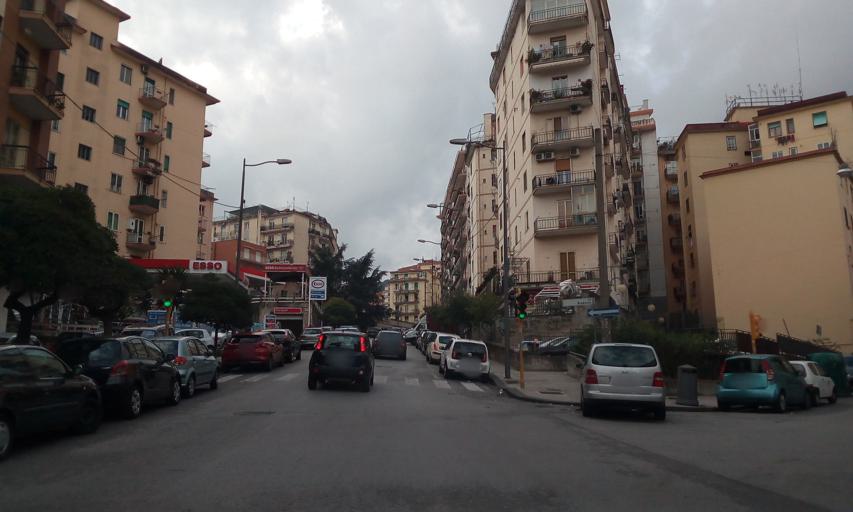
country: IT
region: Campania
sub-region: Provincia di Salerno
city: Capezzano Inferiore
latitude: 40.6843
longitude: 14.7728
